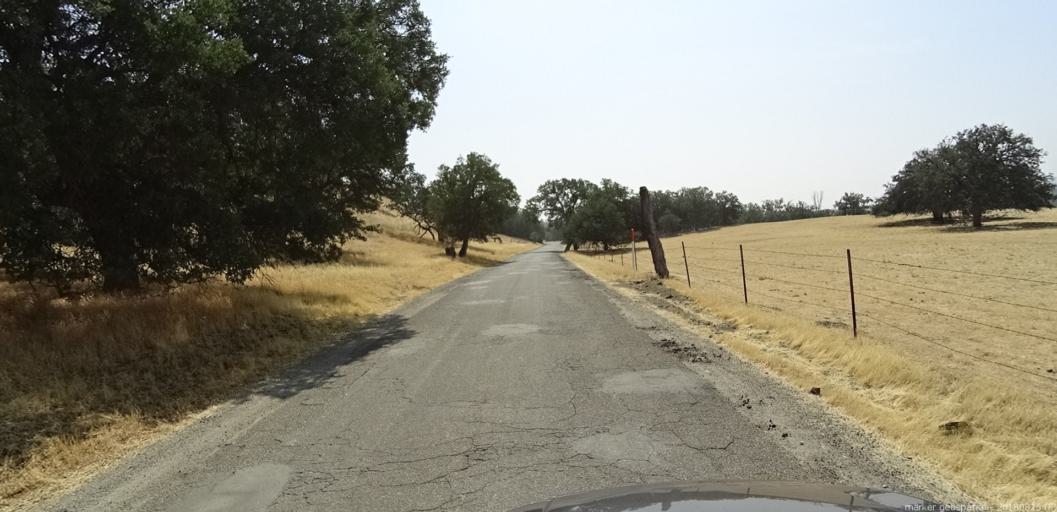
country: US
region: California
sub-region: San Luis Obispo County
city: Shandon
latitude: 35.8754
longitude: -120.4147
